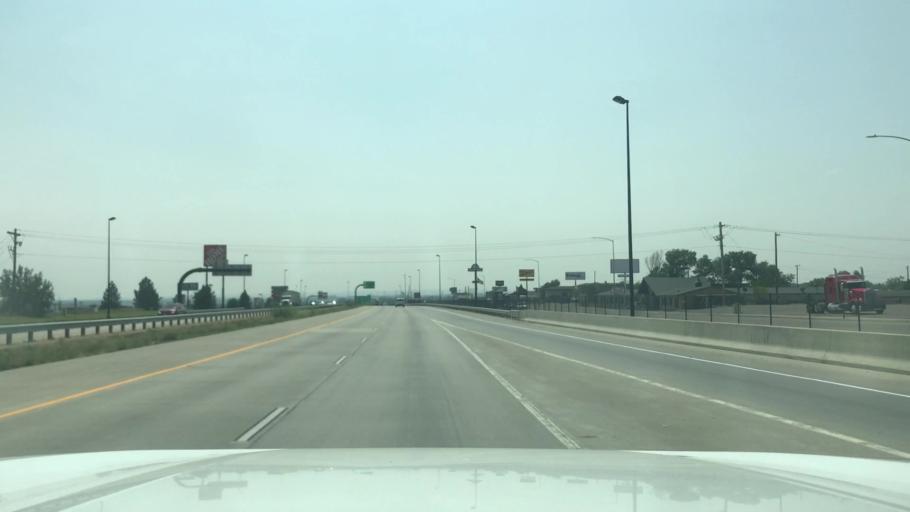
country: US
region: Colorado
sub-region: Pueblo County
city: Pueblo
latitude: 38.3174
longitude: -104.6156
